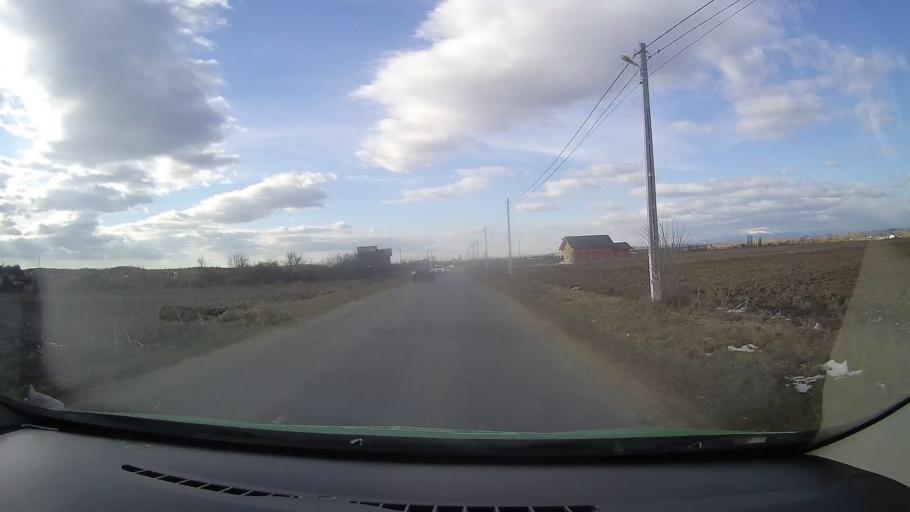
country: RO
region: Dambovita
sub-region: Comuna Ulmi
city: Ulmi
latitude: 44.8965
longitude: 25.5004
